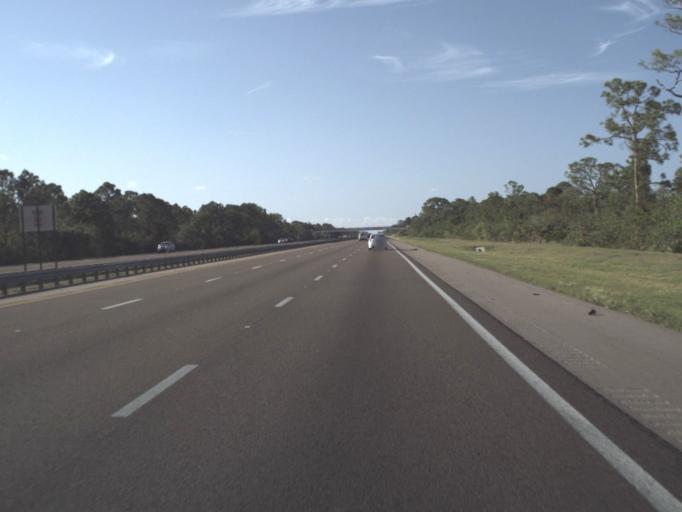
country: US
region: Florida
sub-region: Brevard County
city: Grant-Valkaria
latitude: 27.9181
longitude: -80.6004
